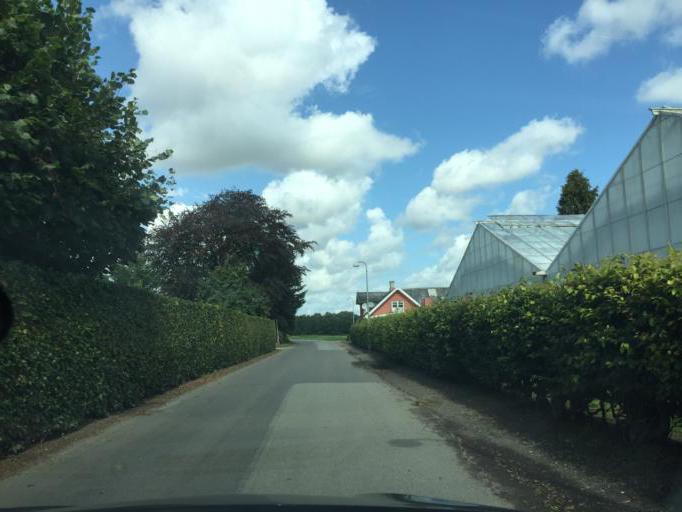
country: DK
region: South Denmark
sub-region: Odense Kommune
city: Stige
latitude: 55.4465
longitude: 10.3901
